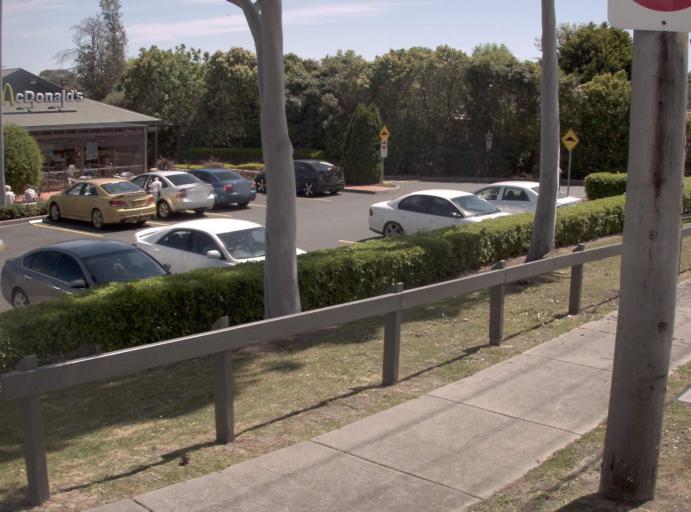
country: AU
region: Victoria
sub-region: Monash
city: Notting Hill
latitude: -37.8864
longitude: 145.1456
